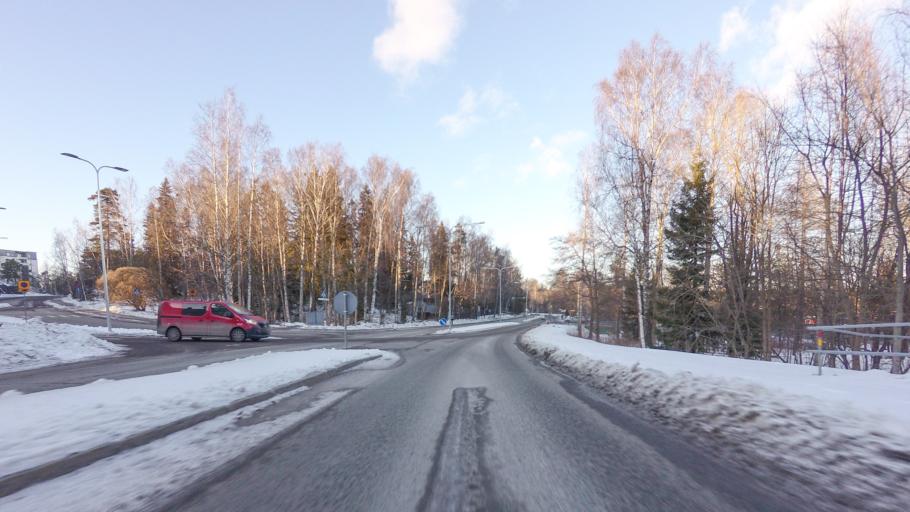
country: FI
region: Uusimaa
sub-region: Helsinki
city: Helsinki
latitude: 60.1677
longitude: 25.0477
